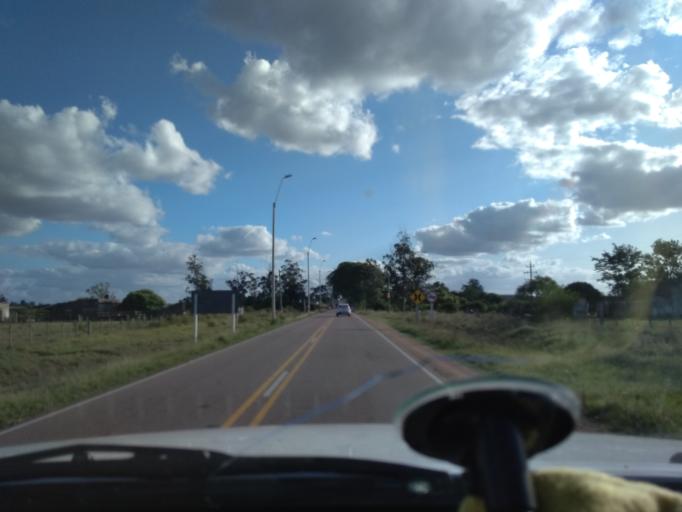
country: UY
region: Canelones
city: Tala
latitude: -34.3636
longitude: -55.7779
